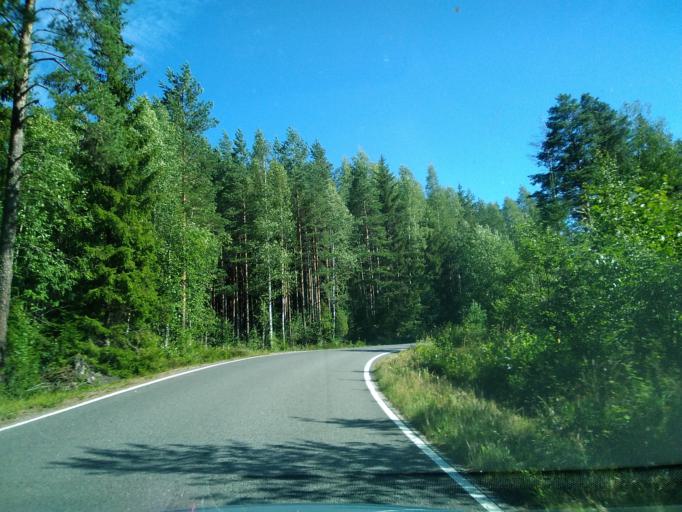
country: FI
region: Uusimaa
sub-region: Helsinki
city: Kaerkoelae
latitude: 60.7774
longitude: 24.0718
